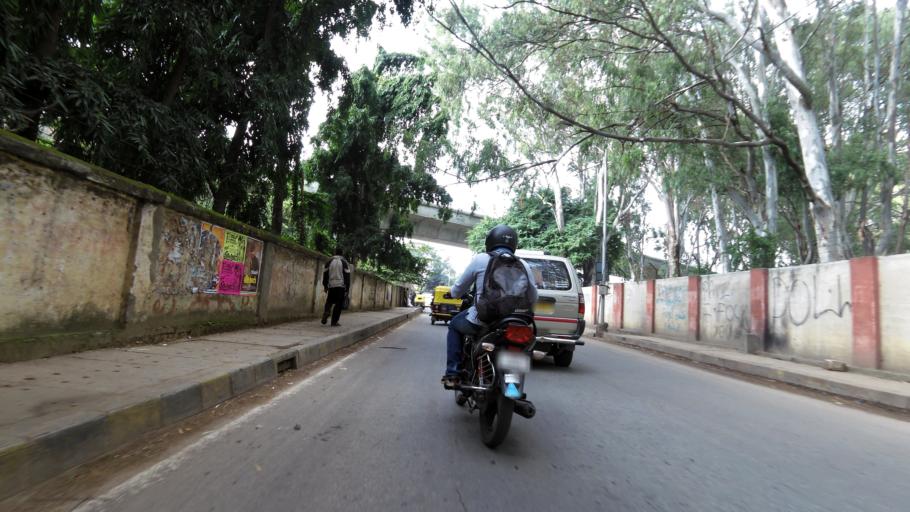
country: IN
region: Karnataka
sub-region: Bangalore Urban
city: Bangalore
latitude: 12.9855
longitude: 77.6426
